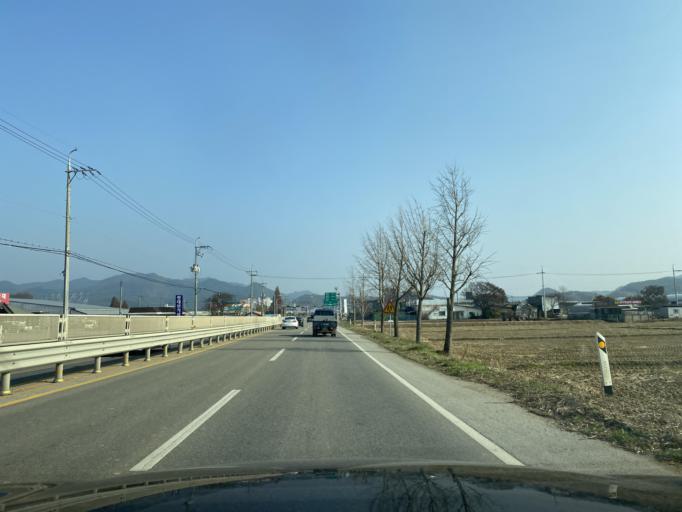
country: KR
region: Chungcheongnam-do
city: Yesan
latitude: 36.6849
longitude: 126.8132
